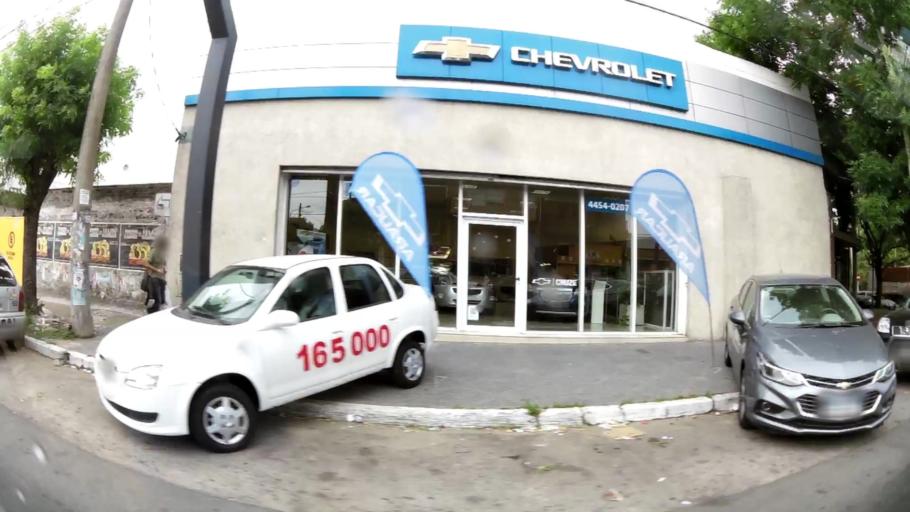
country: AR
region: Buenos Aires
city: San Justo
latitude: -34.6640
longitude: -58.5222
